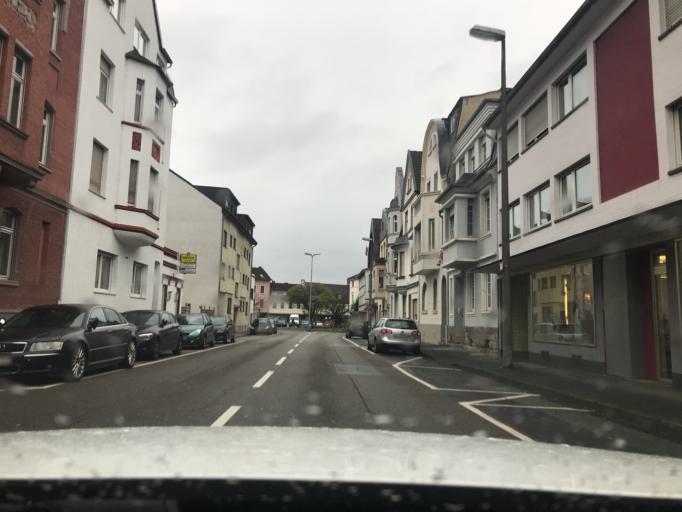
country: DE
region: Rheinland-Pfalz
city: Neuwied
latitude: 50.4339
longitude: 7.4676
